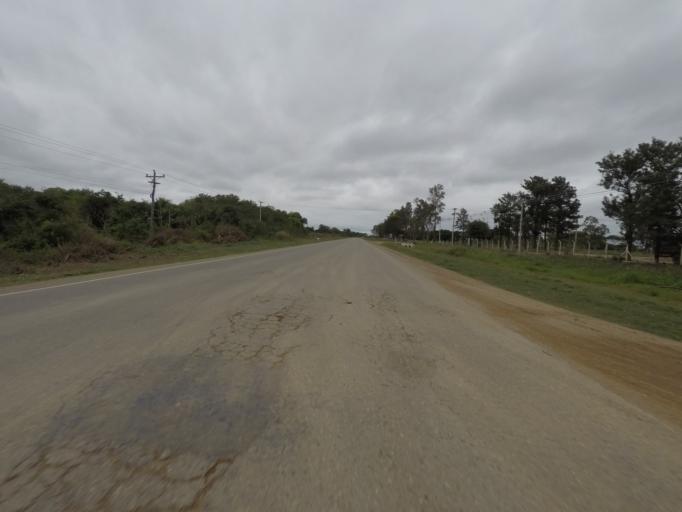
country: BO
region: Santa Cruz
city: Okinawa Numero Uno
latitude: -17.2216
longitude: -62.5561
